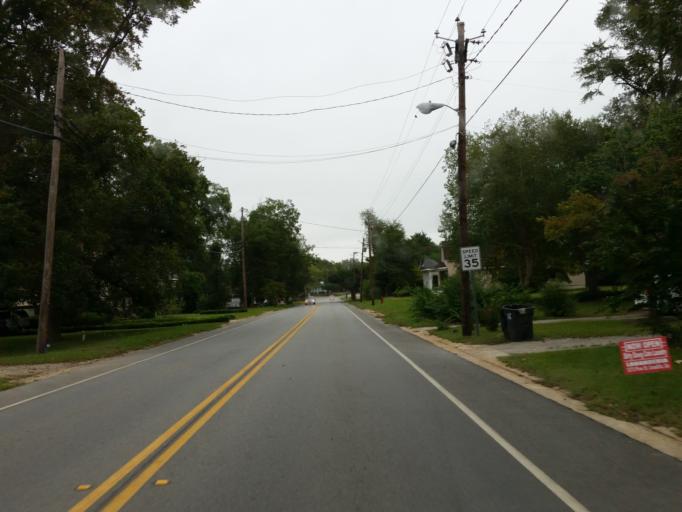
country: US
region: Georgia
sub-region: Dooly County
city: Unadilla
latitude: 32.2604
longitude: -83.7406
